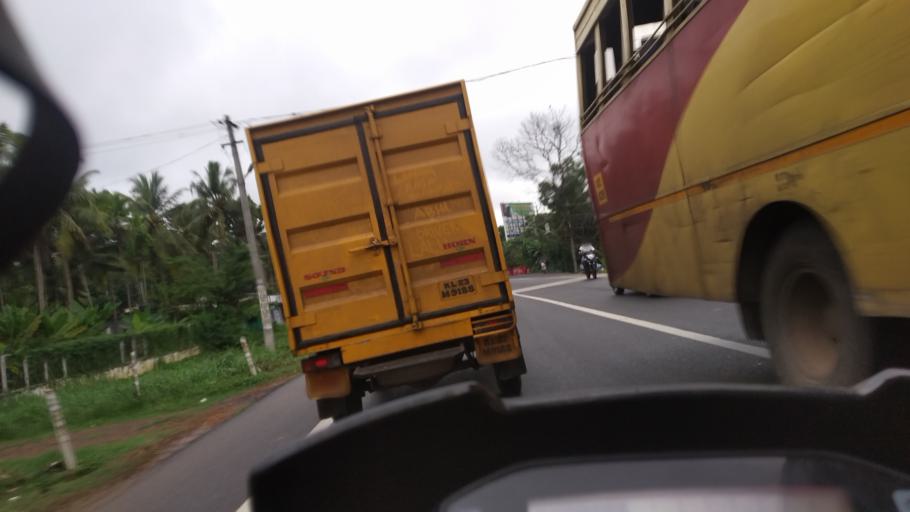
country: IN
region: Kerala
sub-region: Alappuzha
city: Mavelikara
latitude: 9.3170
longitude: 76.4271
